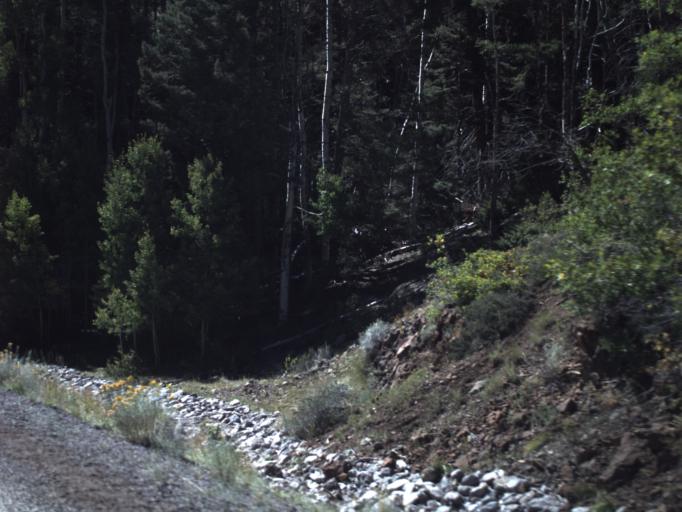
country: US
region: Utah
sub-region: Beaver County
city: Beaver
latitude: 38.2790
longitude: -112.4579
